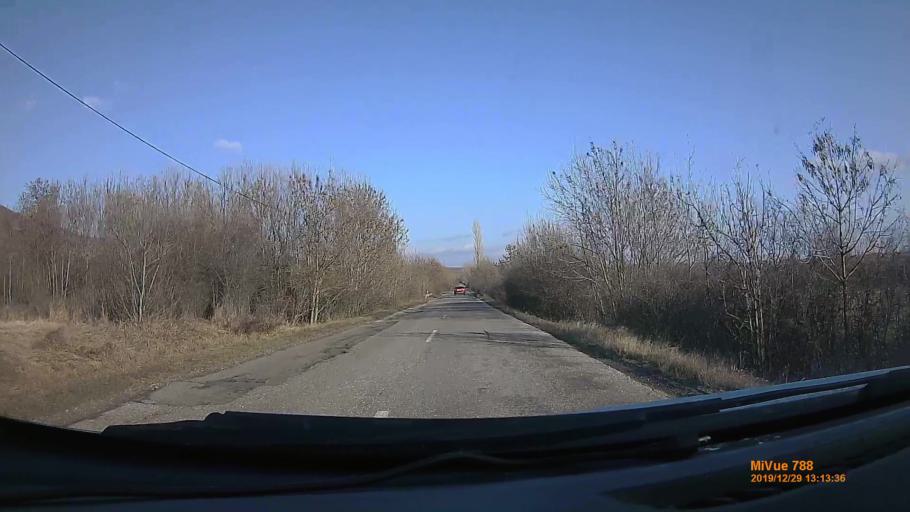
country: HU
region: Heves
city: Domoszlo
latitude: 47.8281
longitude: 20.0847
